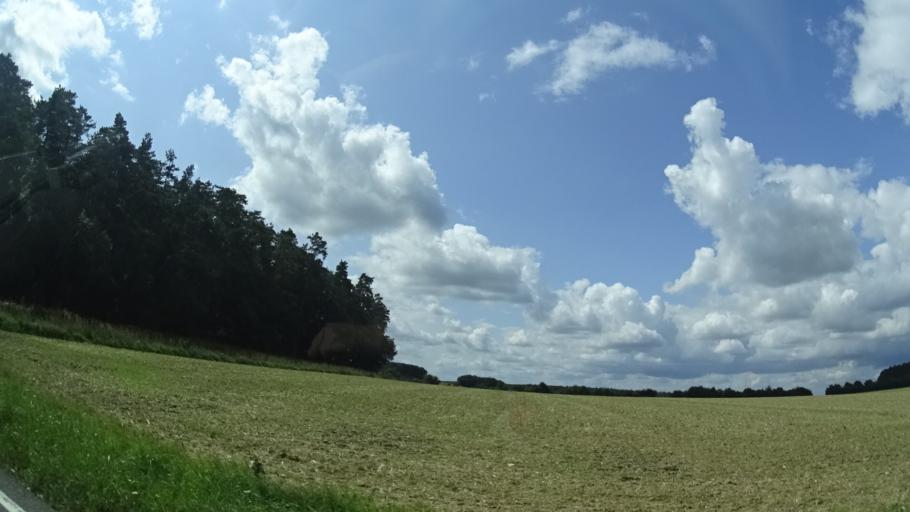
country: DE
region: Bavaria
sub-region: Upper Franconia
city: Neustadt bei Coburg
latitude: 50.2826
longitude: 11.0940
